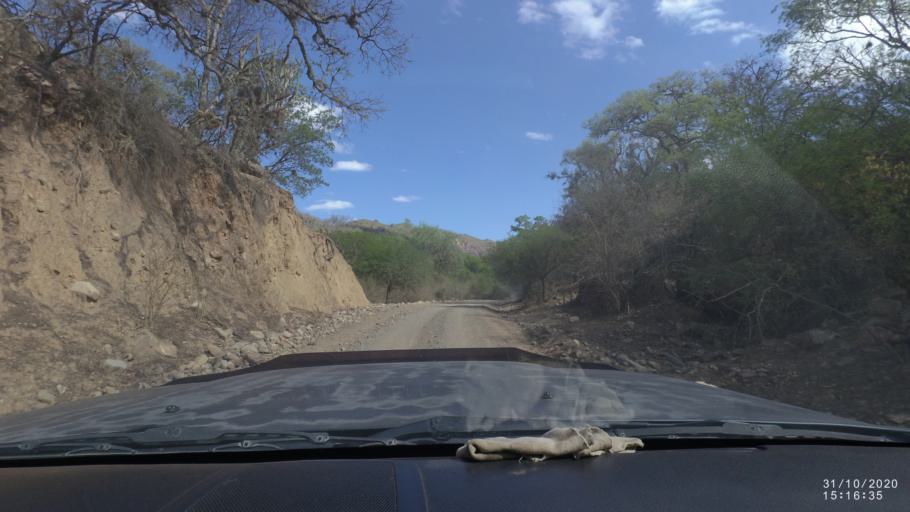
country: BO
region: Cochabamba
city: Aiquile
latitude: -18.3358
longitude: -64.7709
